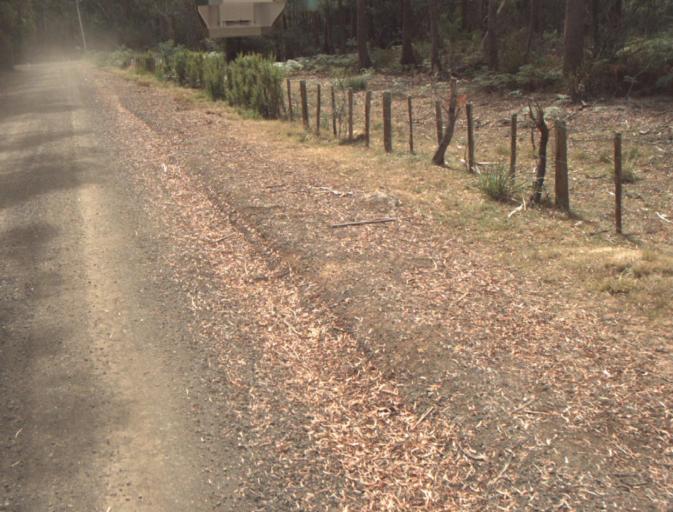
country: AU
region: Tasmania
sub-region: Launceston
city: Mayfield
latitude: -41.2768
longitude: 147.0498
